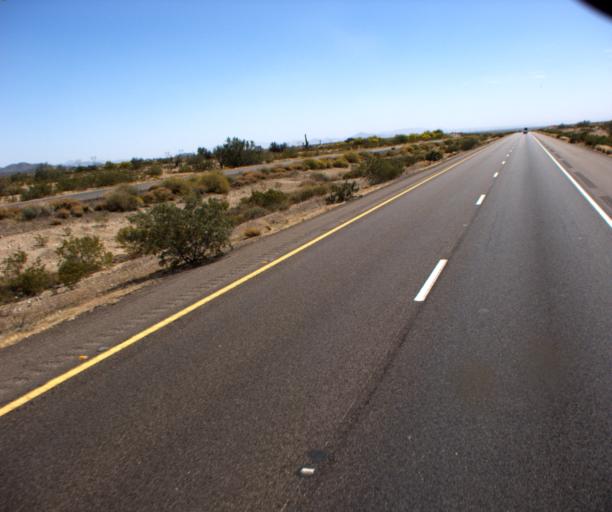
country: US
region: Arizona
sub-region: Maricopa County
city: Gila Bend
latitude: 33.0978
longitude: -112.6494
